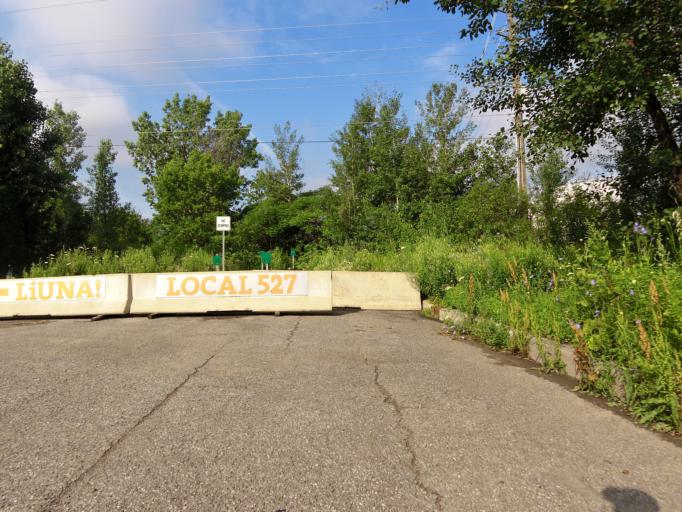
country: CA
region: Ontario
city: Ottawa
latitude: 45.3276
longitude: -75.7145
